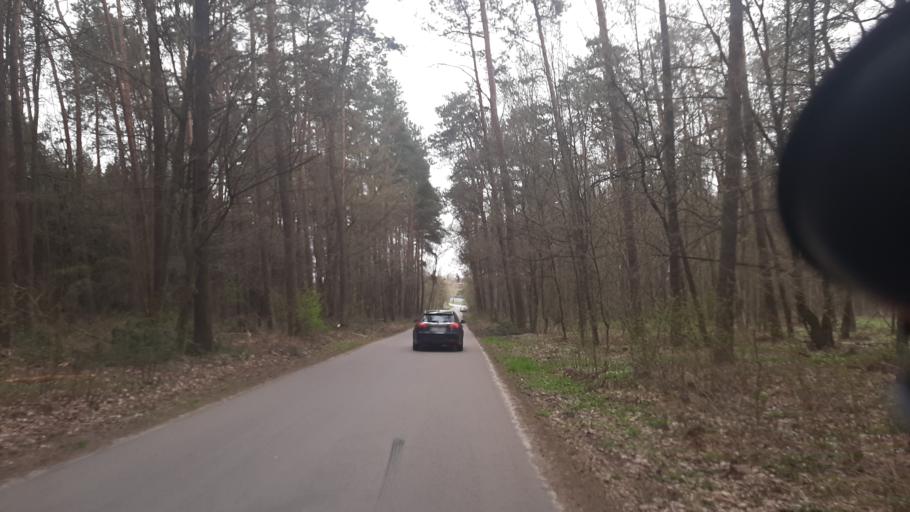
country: PL
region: Lublin Voivodeship
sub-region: Powiat lubelski
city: Niemce
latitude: 51.3707
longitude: 22.5525
